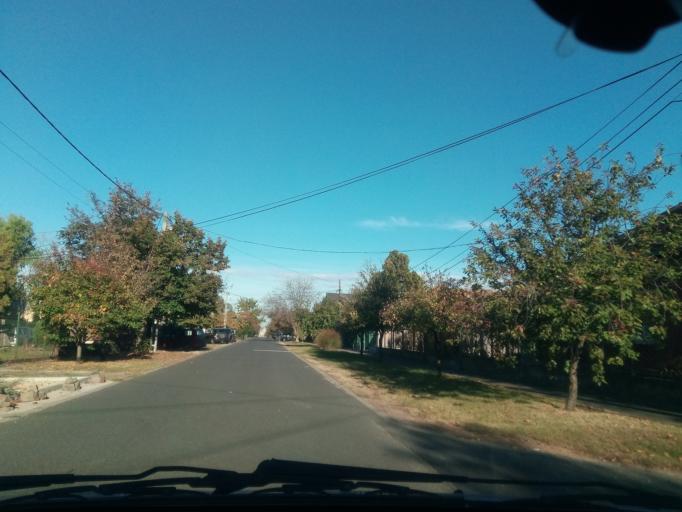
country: HU
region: Pest
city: Gyal
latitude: 47.4298
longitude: 19.2273
